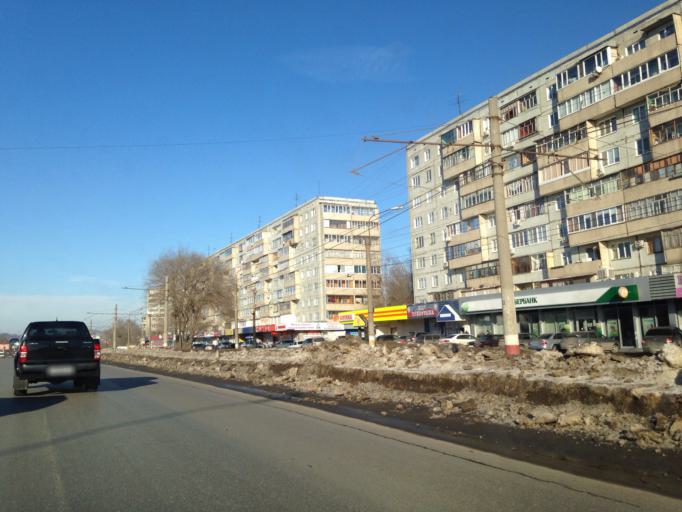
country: RU
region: Ulyanovsk
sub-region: Ulyanovskiy Rayon
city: Ulyanovsk
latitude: 54.3184
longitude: 48.3569
